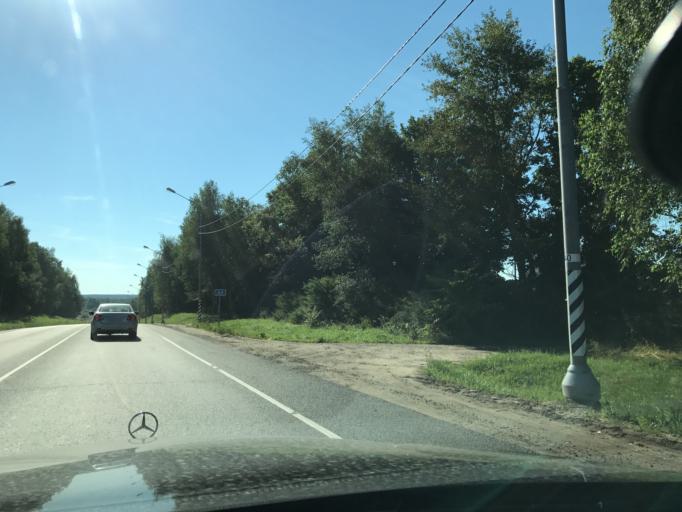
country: RU
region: Moskovskaya
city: Noginsk-9
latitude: 56.1081
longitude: 38.6240
